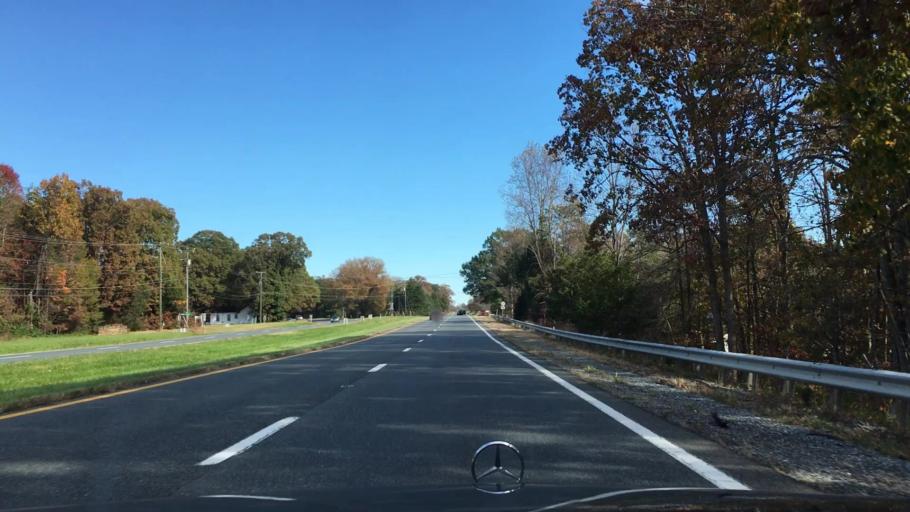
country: US
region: Virginia
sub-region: Campbell County
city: Altavista
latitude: 37.1583
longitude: -79.2245
